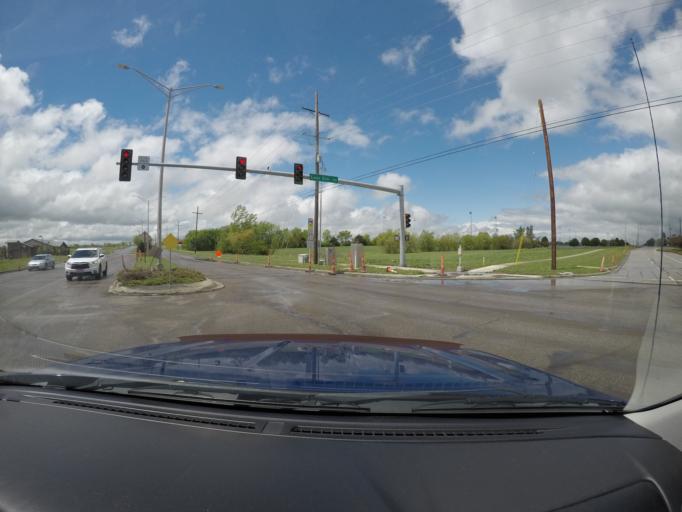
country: US
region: Kansas
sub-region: Johnson County
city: Olathe
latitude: 38.9273
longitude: -94.8347
